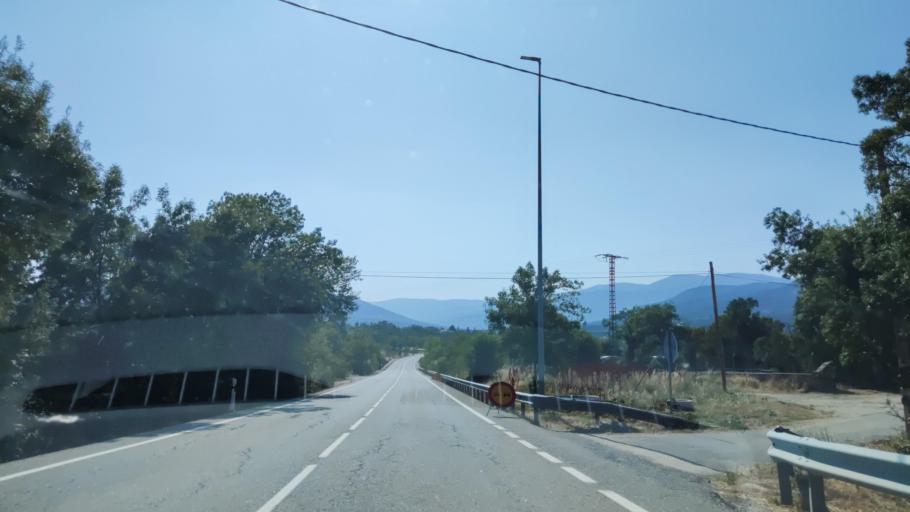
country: ES
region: Madrid
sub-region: Provincia de Madrid
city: Garganta de los Montes
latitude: 40.9420
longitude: -3.7023
